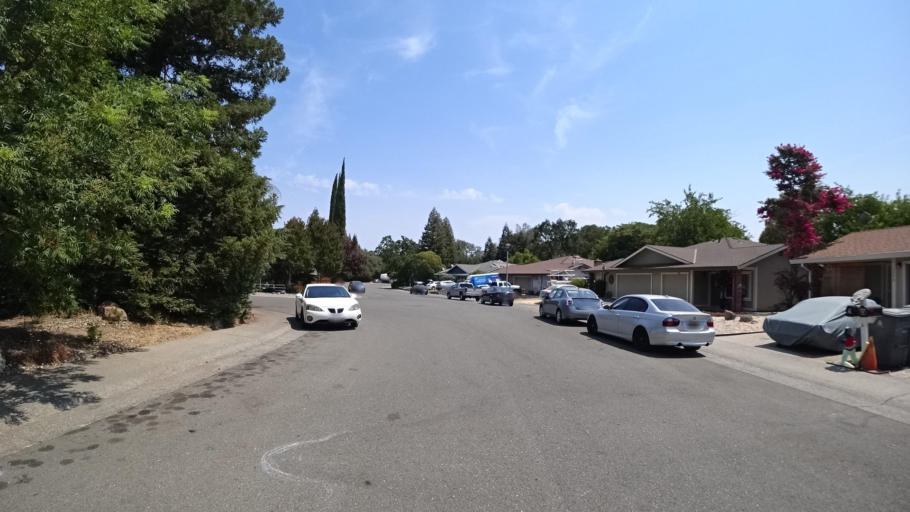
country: US
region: California
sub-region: Placer County
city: Rocklin
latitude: 38.7985
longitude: -121.2348
